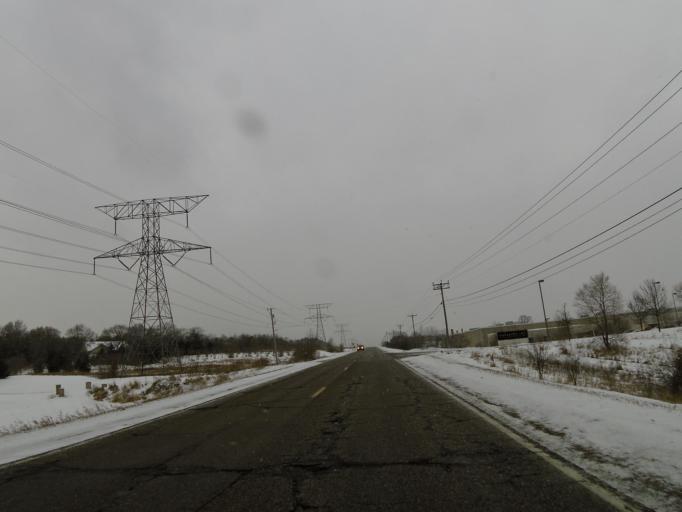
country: US
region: Minnesota
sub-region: Washington County
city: Afton
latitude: 44.9469
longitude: -92.8277
